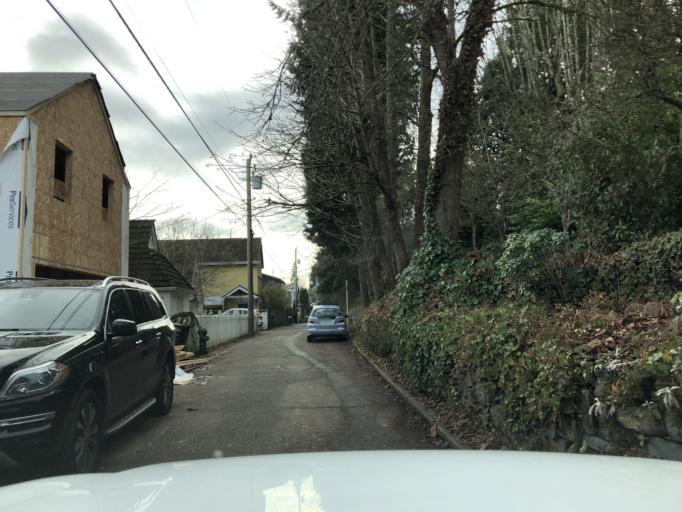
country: US
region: Washington
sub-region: King County
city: Lake Forest Park
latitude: 47.7127
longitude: -122.2769
